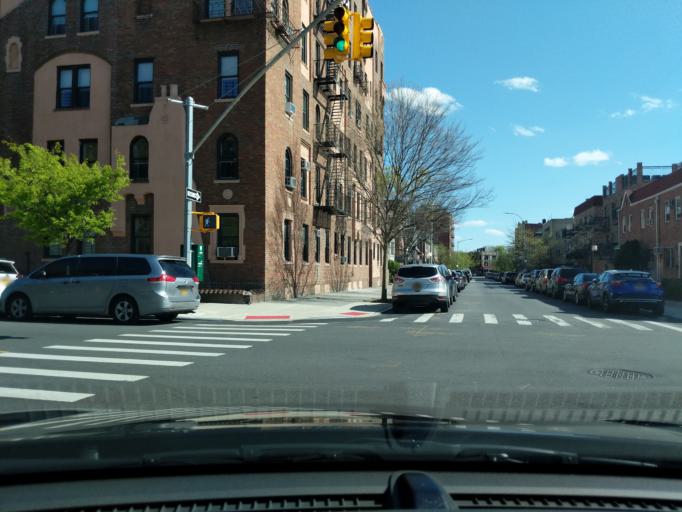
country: US
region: New York
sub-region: Kings County
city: Brooklyn
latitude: 40.6333
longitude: -73.9764
